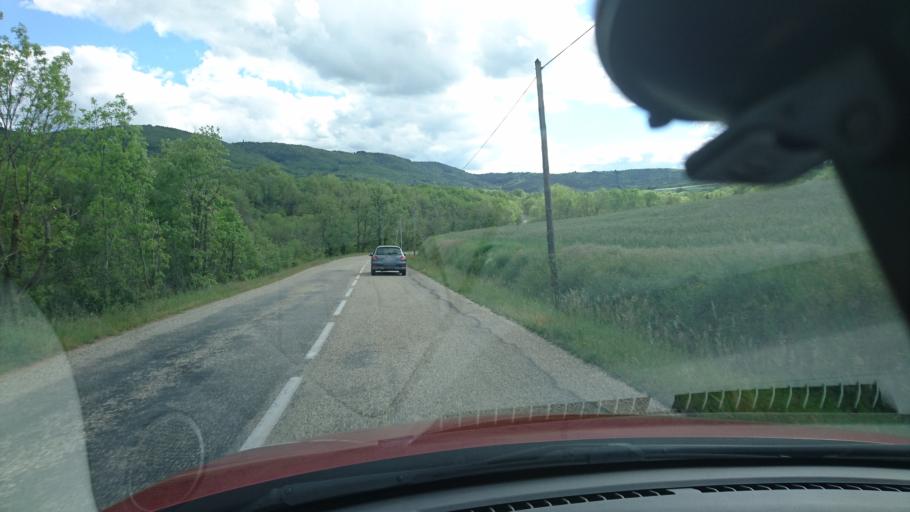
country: FR
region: Rhone-Alpes
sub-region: Departement de la Loire
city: Maclas
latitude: 45.3436
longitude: 4.6890
